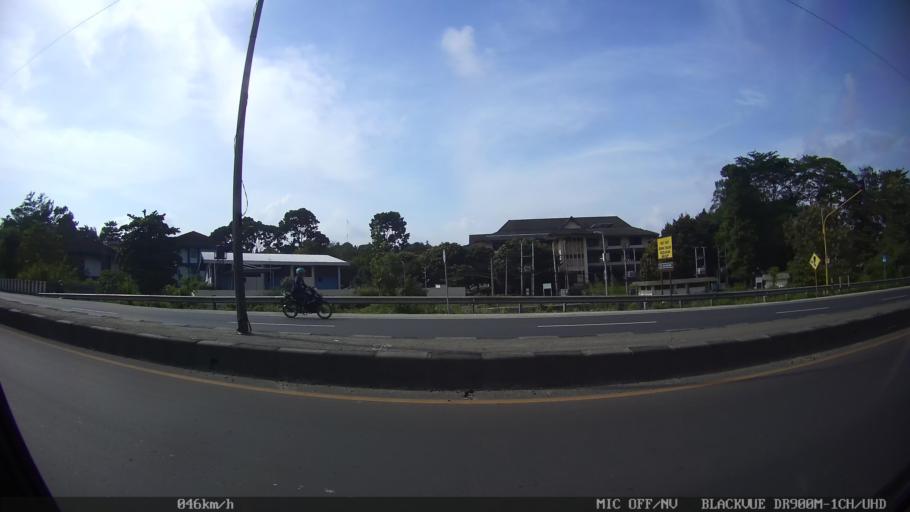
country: ID
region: Lampung
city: Kedaton
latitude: -5.3606
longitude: 105.2401
